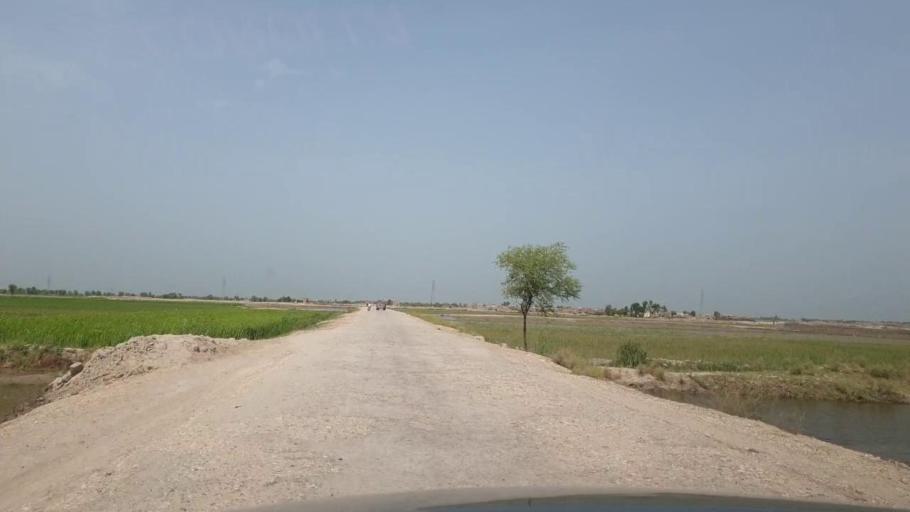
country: PK
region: Sindh
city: Garhi Yasin
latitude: 27.8541
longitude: 68.4325
